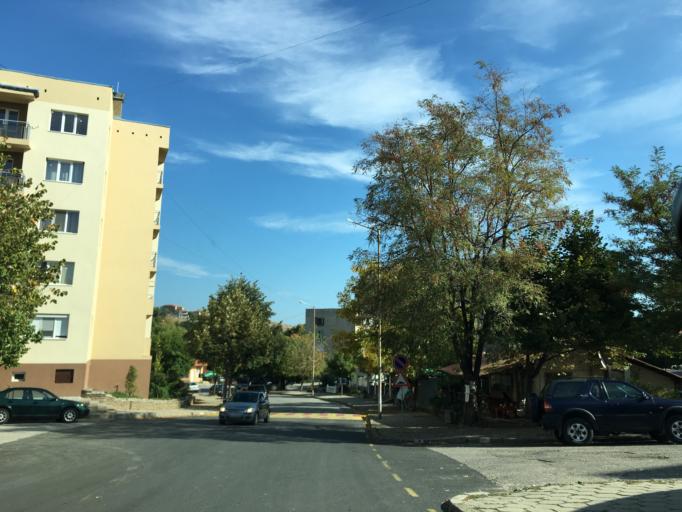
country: BG
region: Khaskovo
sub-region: Obshtina Ivaylovgrad
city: Ivaylovgrad
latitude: 41.5228
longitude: 26.1197
